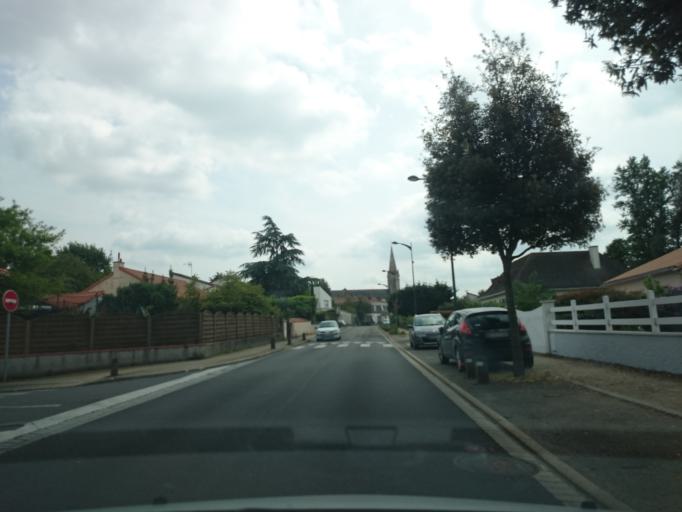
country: FR
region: Pays de la Loire
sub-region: Departement de la Loire-Atlantique
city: La Chevroliere
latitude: 47.0963
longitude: -1.6113
